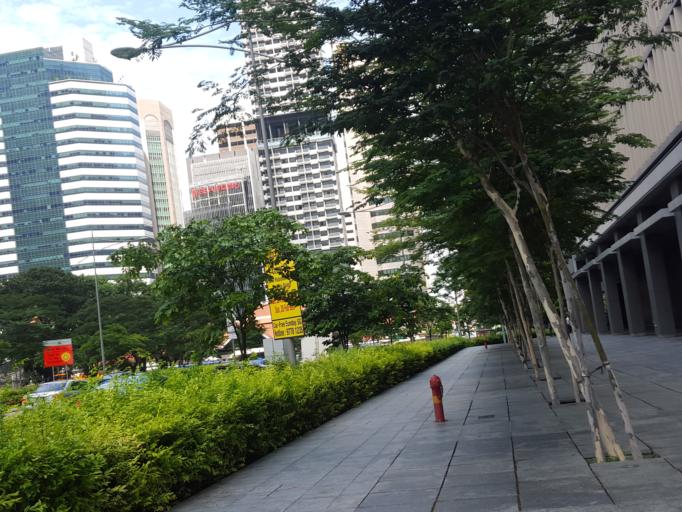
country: SG
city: Singapore
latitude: 1.2801
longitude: 103.8524
